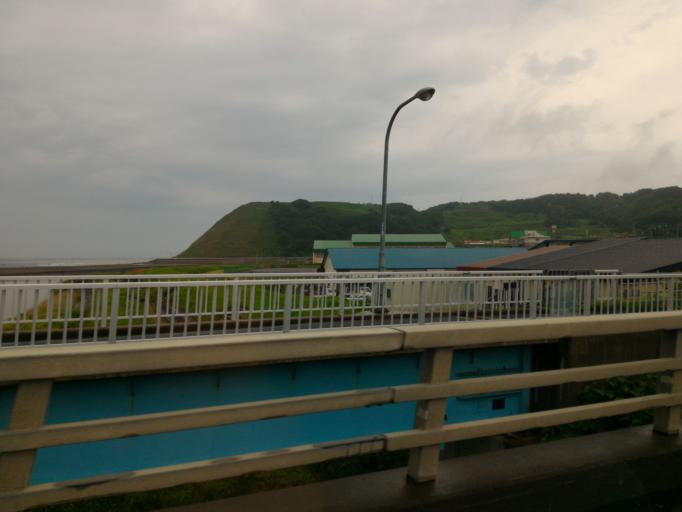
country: JP
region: Hokkaido
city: Rumoi
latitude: 44.0242
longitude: 141.6654
